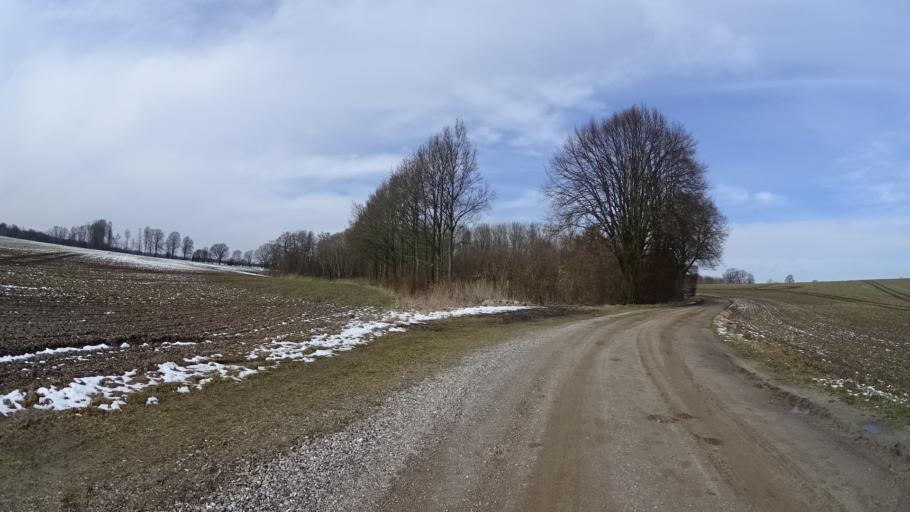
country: DE
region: Schleswig-Holstein
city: Loptin
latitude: 54.1628
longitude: 10.2288
